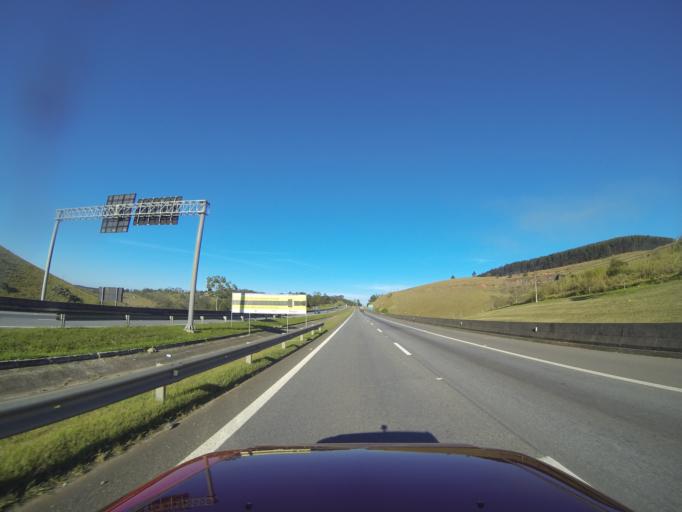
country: BR
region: Sao Paulo
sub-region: Santa Isabel
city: Santa Isabel
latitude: -23.2006
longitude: -46.1727
